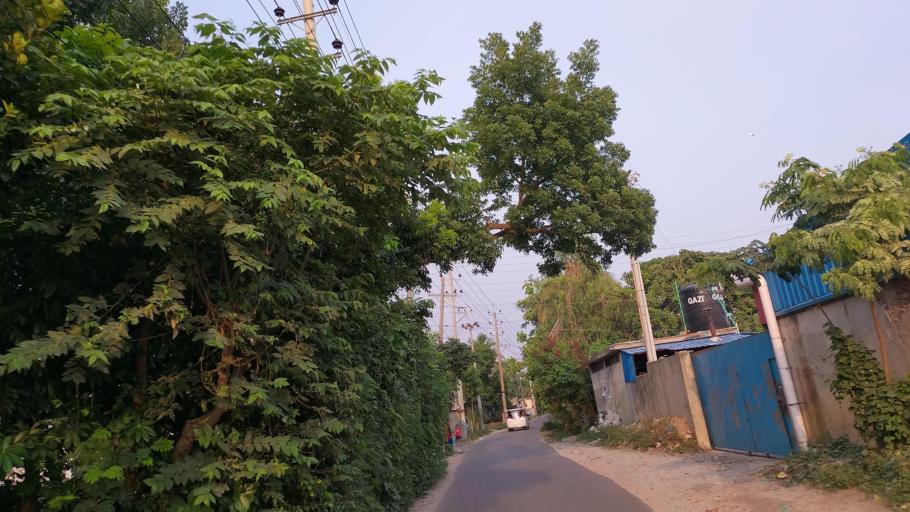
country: BD
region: Dhaka
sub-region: Dhaka
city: Dhaka
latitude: 23.6540
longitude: 90.3442
